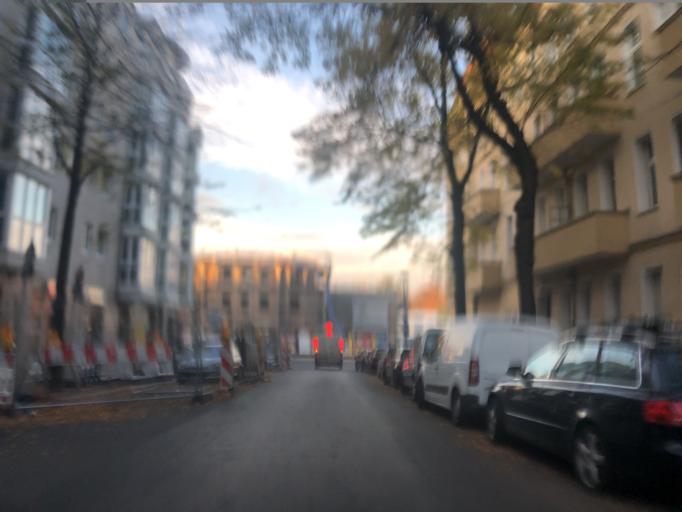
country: DE
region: Berlin
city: Weissensee
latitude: 52.5501
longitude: 13.4627
